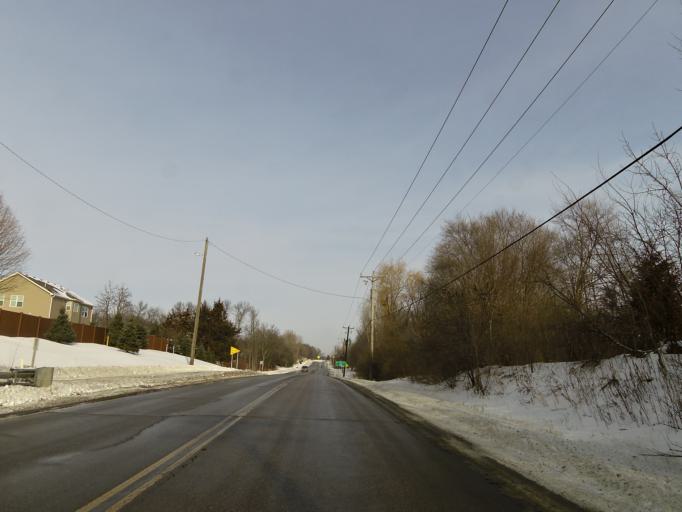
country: US
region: Minnesota
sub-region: Carver County
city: Chanhassen
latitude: 44.8850
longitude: -93.5207
